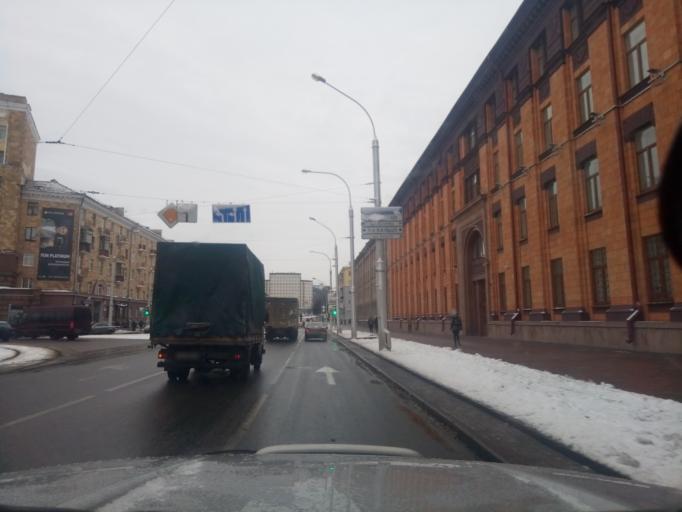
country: BY
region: Minsk
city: Minsk
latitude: 53.9081
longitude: 27.5823
